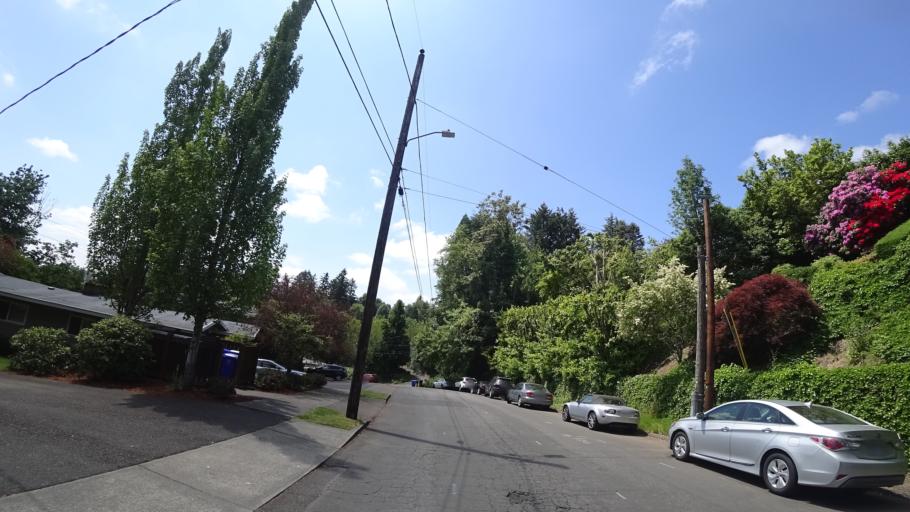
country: US
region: Oregon
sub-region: Multnomah County
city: Portland
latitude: 45.4713
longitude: -122.6916
